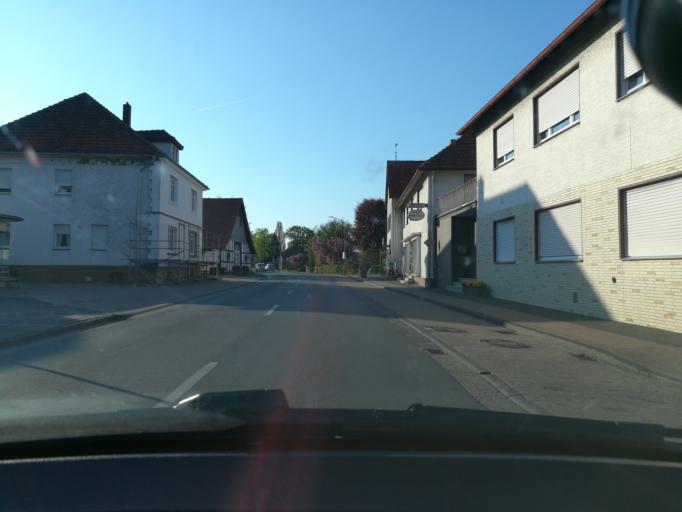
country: DE
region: North Rhine-Westphalia
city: Versmold
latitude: 52.0332
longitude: 8.1987
